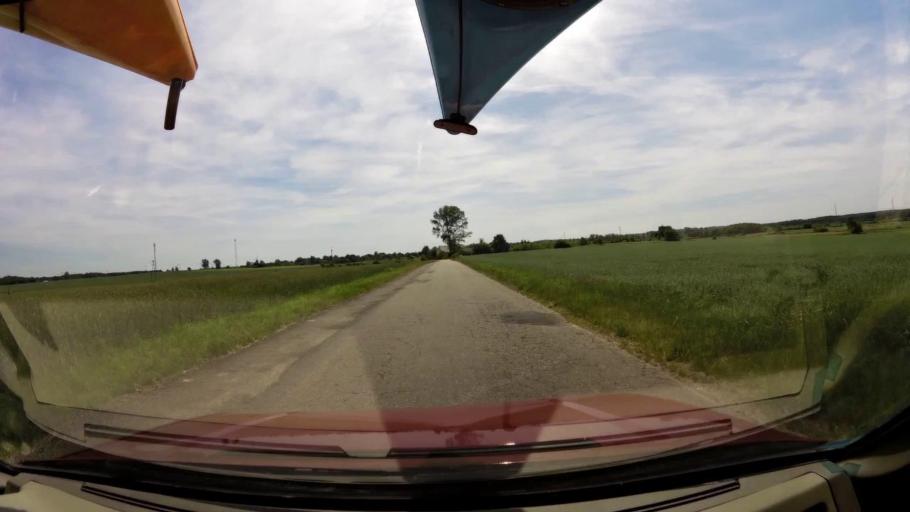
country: PL
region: West Pomeranian Voivodeship
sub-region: Powiat slawienski
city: Darlowo
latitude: 54.3237
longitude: 16.3962
